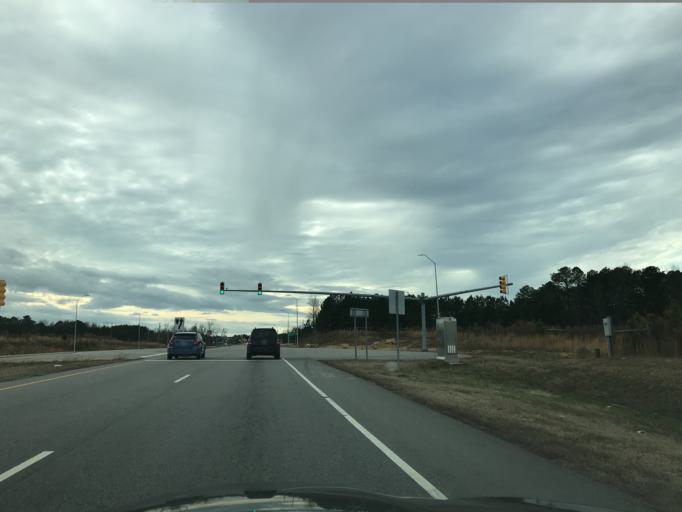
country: US
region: North Carolina
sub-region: Wake County
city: Rolesville
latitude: 35.9155
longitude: -78.4479
